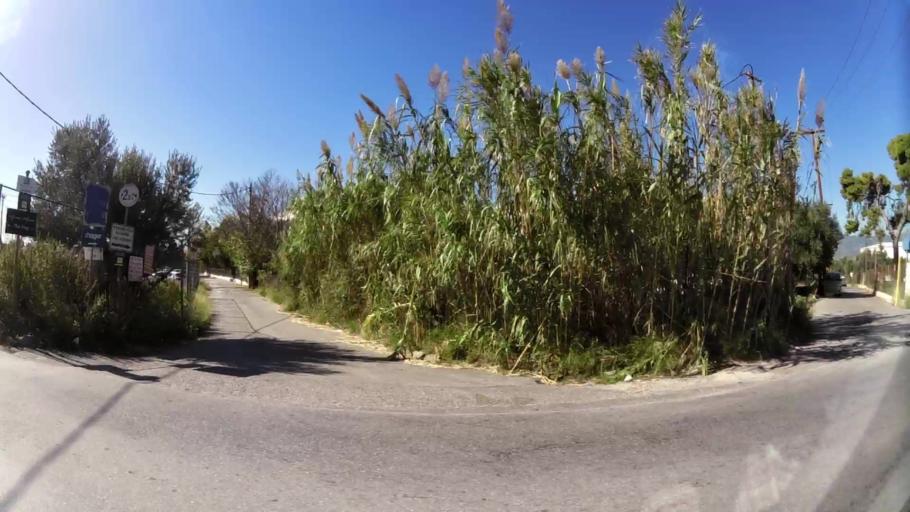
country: GR
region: Attica
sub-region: Nomarchia Athinas
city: Lykovrysi
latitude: 38.0820
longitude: 23.7919
